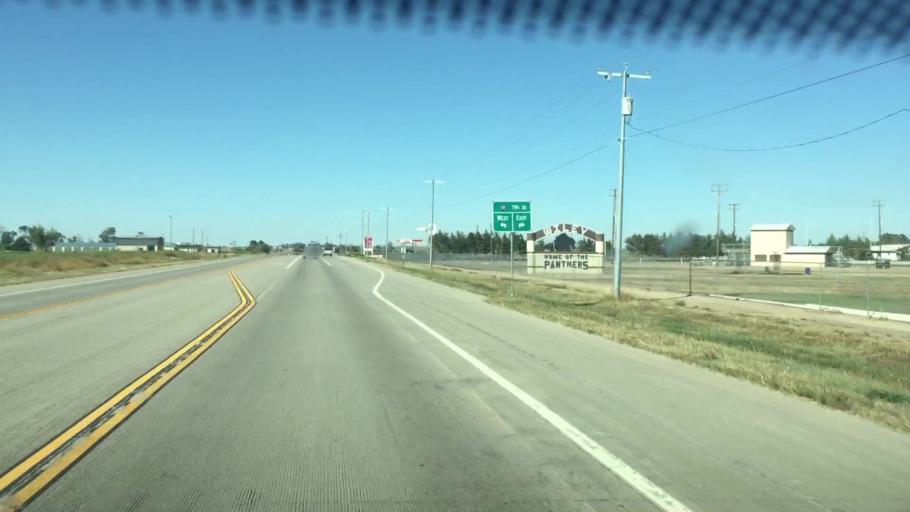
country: US
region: Colorado
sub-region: Prowers County
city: Lamar
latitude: 38.1554
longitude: -102.7237
